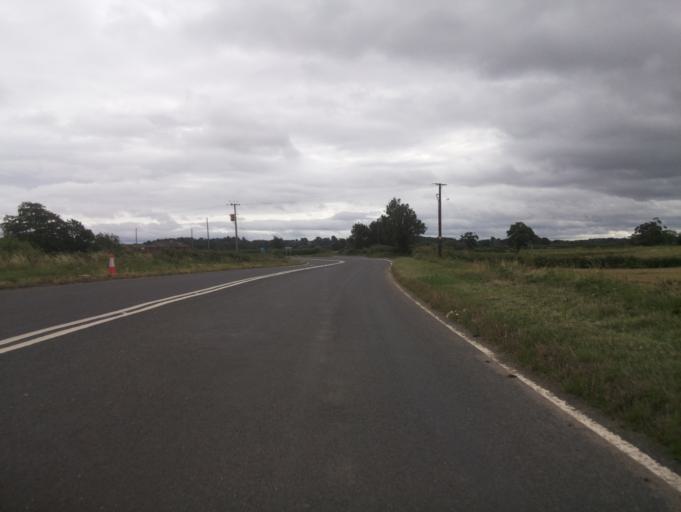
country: GB
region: England
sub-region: Worcestershire
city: Kempsey
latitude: 52.1050
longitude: -2.2186
